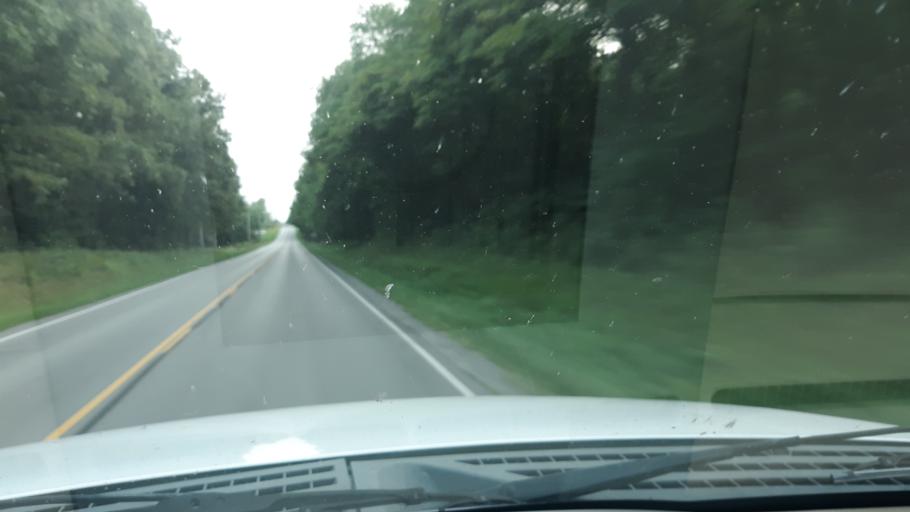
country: US
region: Illinois
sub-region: White County
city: Norris City
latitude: 37.9605
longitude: -88.3348
